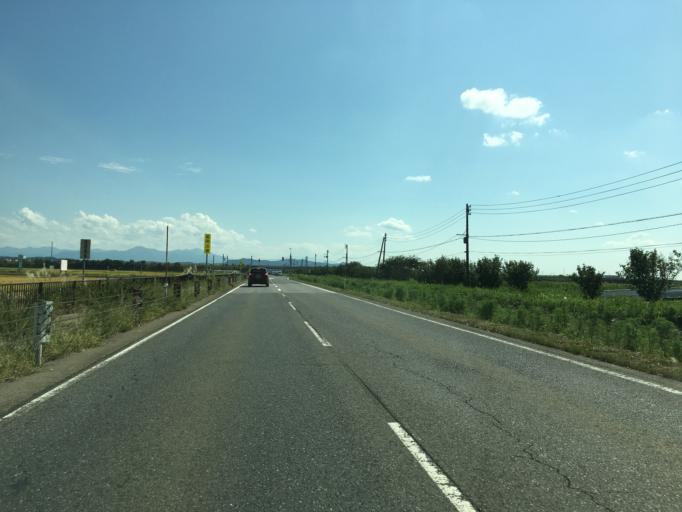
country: JP
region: Niigata
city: Niitsu-honcho
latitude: 37.8270
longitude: 139.0979
